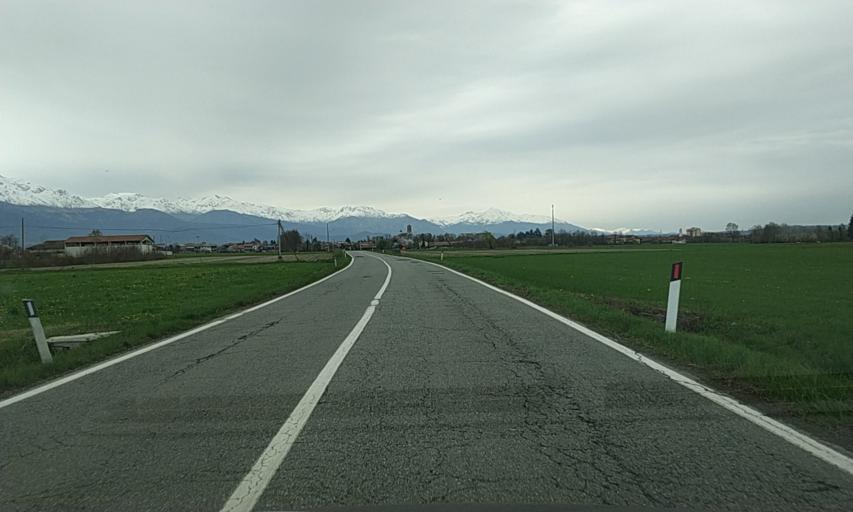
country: IT
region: Piedmont
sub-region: Provincia di Torino
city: Favria
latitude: 45.3201
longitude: 7.6832
